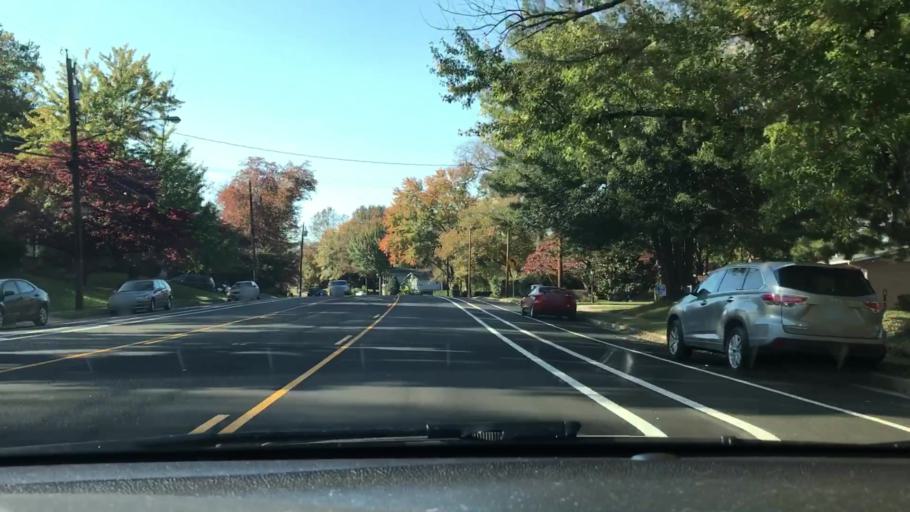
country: US
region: Virginia
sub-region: Fairfax County
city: Annandale
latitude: 38.8397
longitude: -77.1957
